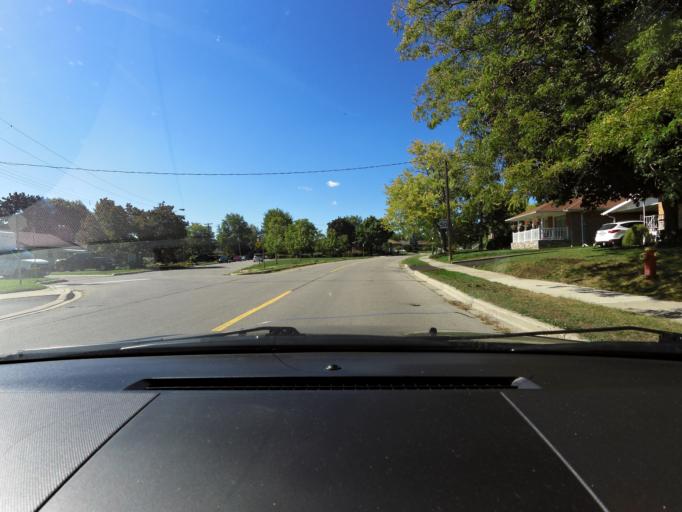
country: CA
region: Ontario
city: Burlington
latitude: 43.3476
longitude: -79.8196
